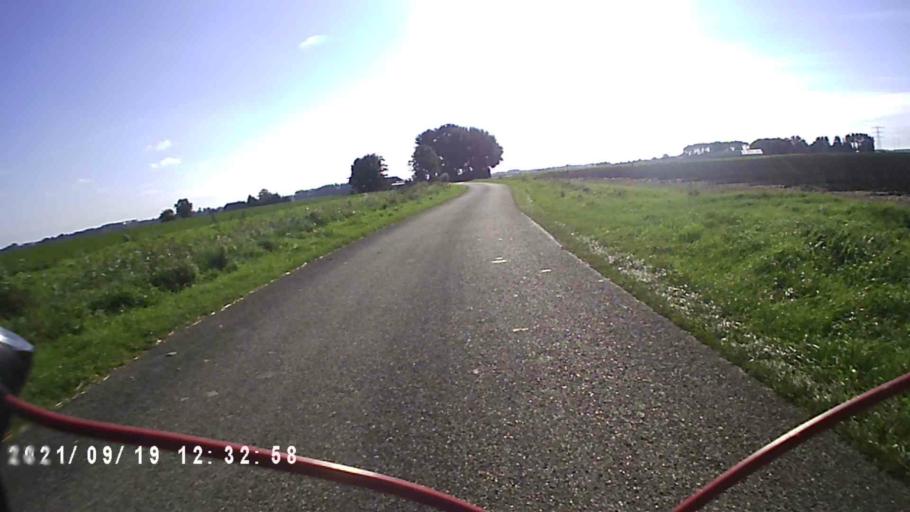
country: NL
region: Groningen
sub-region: Gemeente Slochteren
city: Slochteren
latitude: 53.2200
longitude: 6.9040
